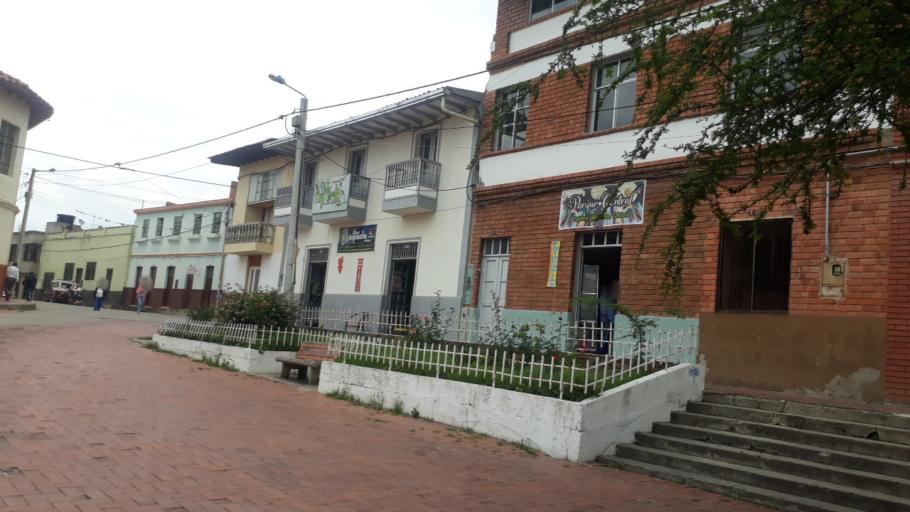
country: CO
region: Boyaca
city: Soata
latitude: 6.3348
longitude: -72.6808
